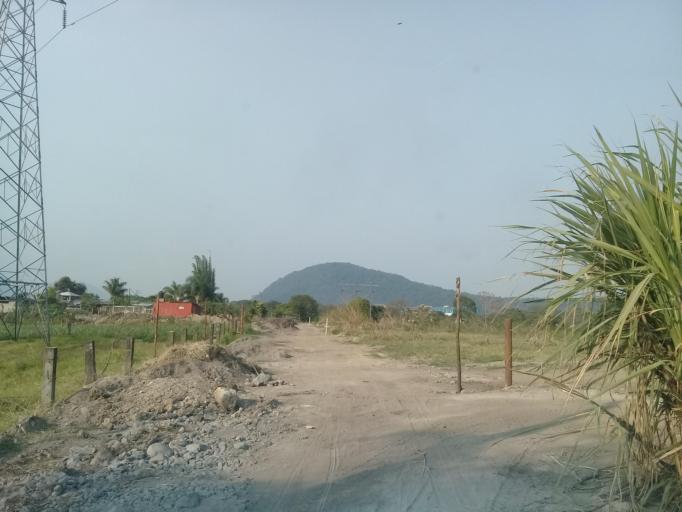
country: MX
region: Veracruz
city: Ixtac Zoquitlan
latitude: 18.8578
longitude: -97.0526
